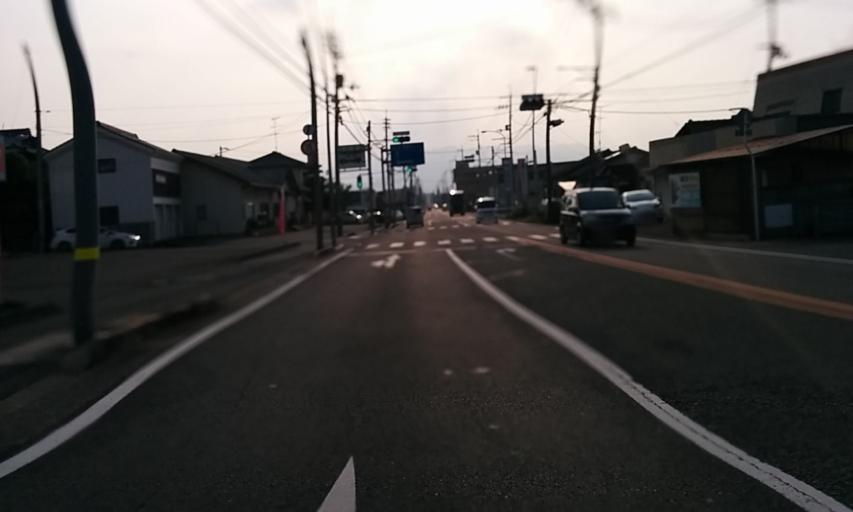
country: JP
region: Ehime
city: Saijo
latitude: 33.8946
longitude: 133.1577
